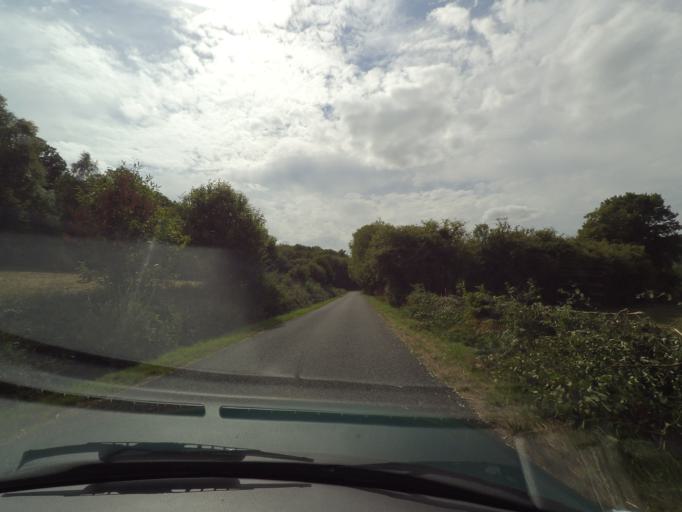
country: FR
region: Limousin
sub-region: Departement de la Haute-Vienne
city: Ladignac-le-Long
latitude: 45.6482
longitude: 1.1110
